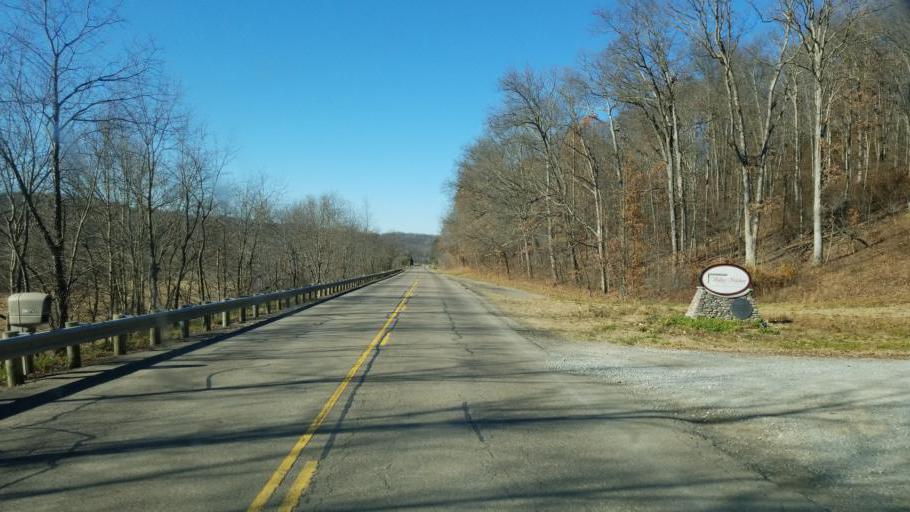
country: US
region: Ohio
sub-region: Knox County
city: Oak Hill
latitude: 40.3552
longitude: -82.2248
